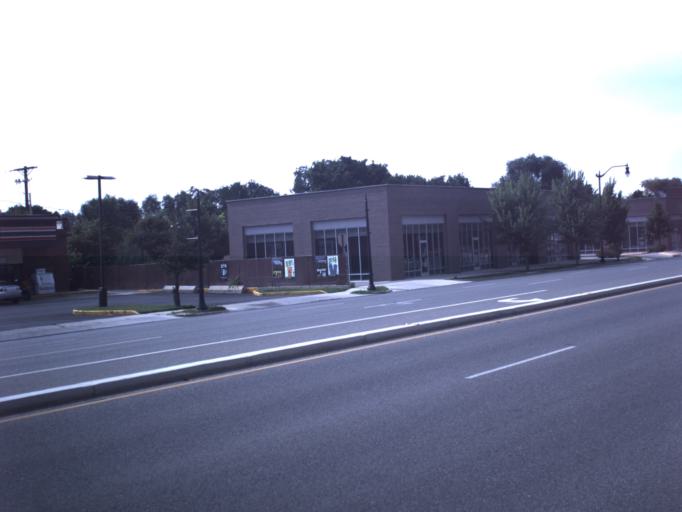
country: US
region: Utah
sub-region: Salt Lake County
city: Salt Lake City
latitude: 40.7804
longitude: -111.8996
